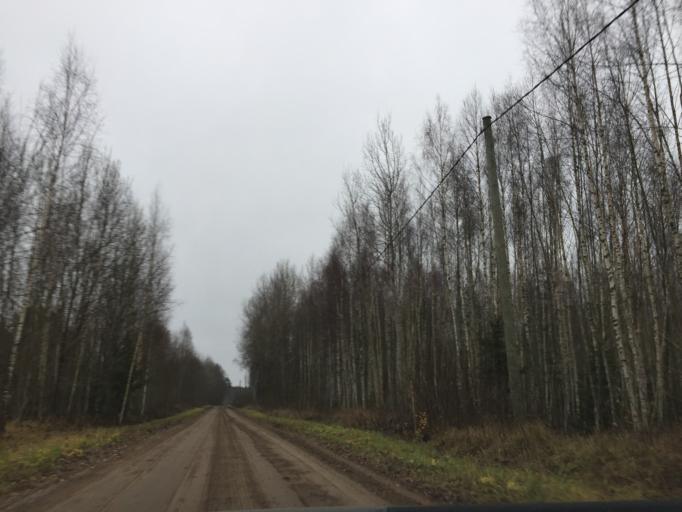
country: LV
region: Limbazu Rajons
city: Limbazi
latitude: 57.5029
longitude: 24.7648
